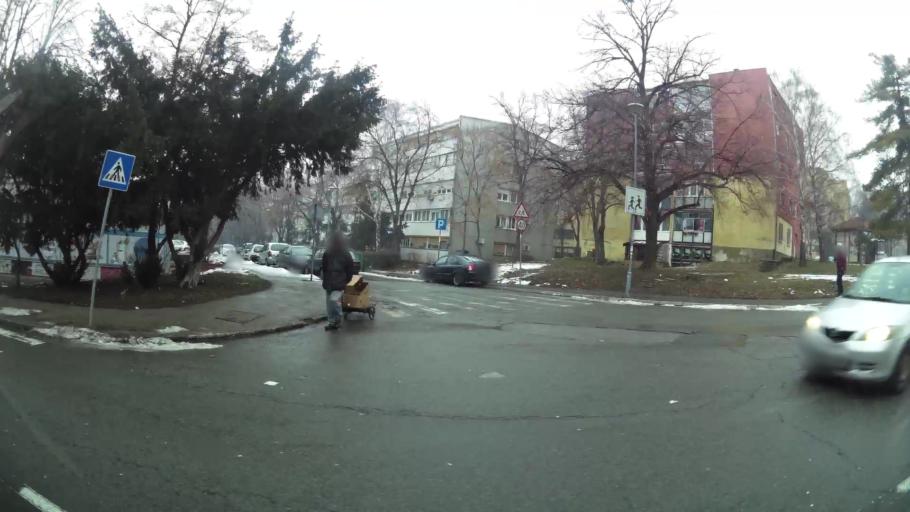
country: RS
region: Central Serbia
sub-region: Belgrade
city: Vozdovac
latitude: 44.7682
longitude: 20.4955
